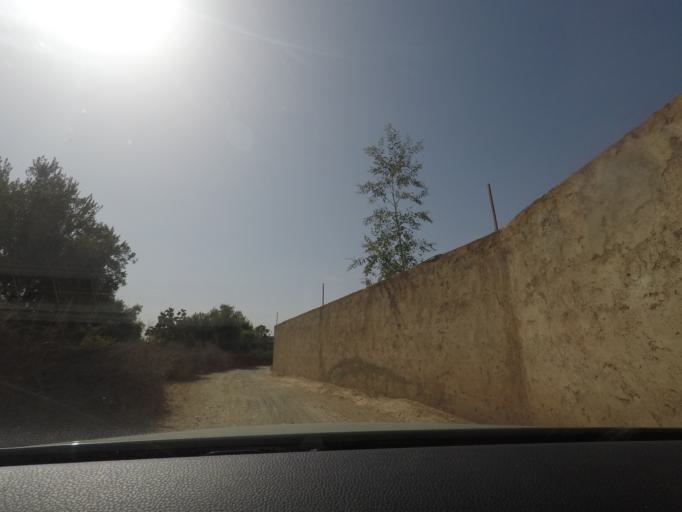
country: MA
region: Marrakech-Tensift-Al Haouz
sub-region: Marrakech
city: Marrakesh
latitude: 31.5788
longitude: -8.0280
